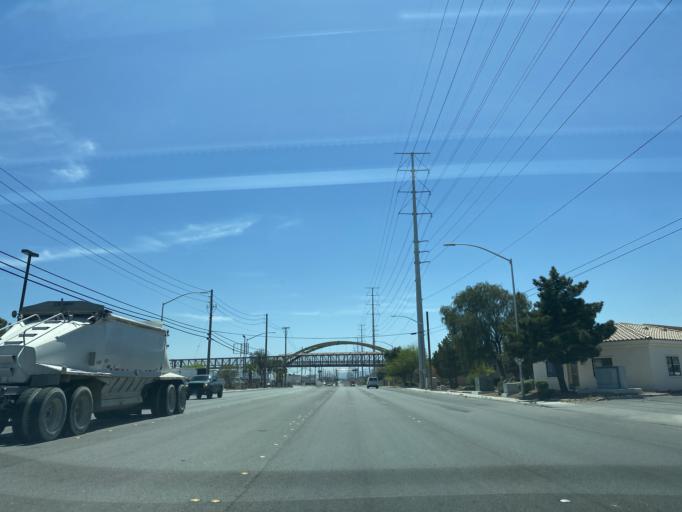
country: US
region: Nevada
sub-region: Clark County
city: North Las Vegas
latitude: 36.2286
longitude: -115.1193
